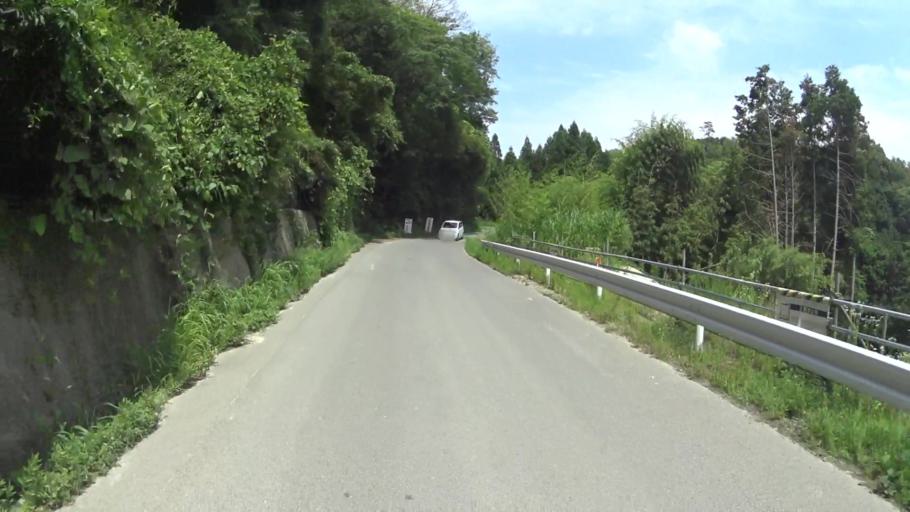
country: JP
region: Mie
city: Ueno-ebisumachi
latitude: 34.8055
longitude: 136.1292
